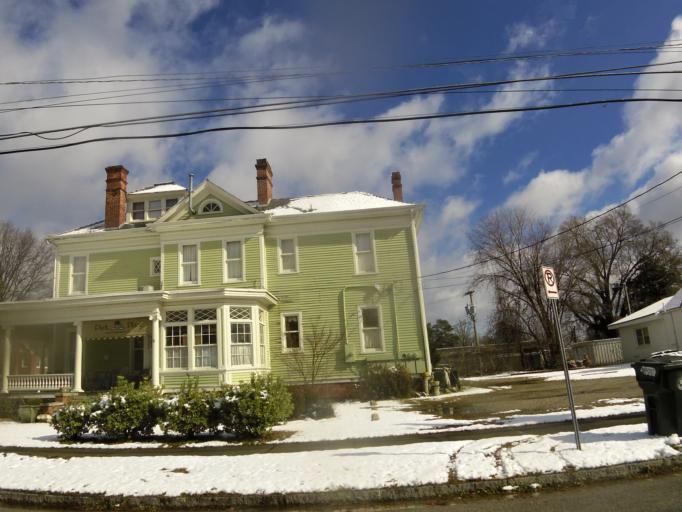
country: US
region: North Carolina
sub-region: Wilson County
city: Wilson
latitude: 35.7285
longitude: -77.9159
